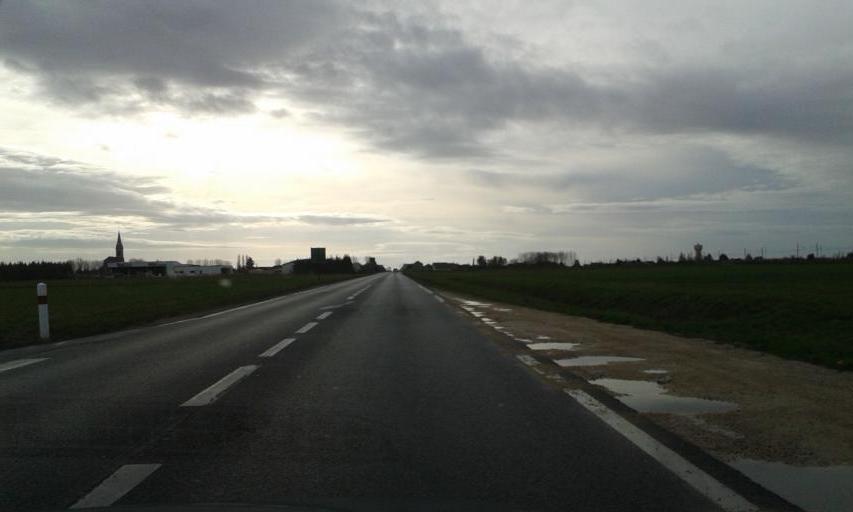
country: FR
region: Centre
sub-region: Departement du Loiret
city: Baule
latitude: 47.8171
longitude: 1.6788
